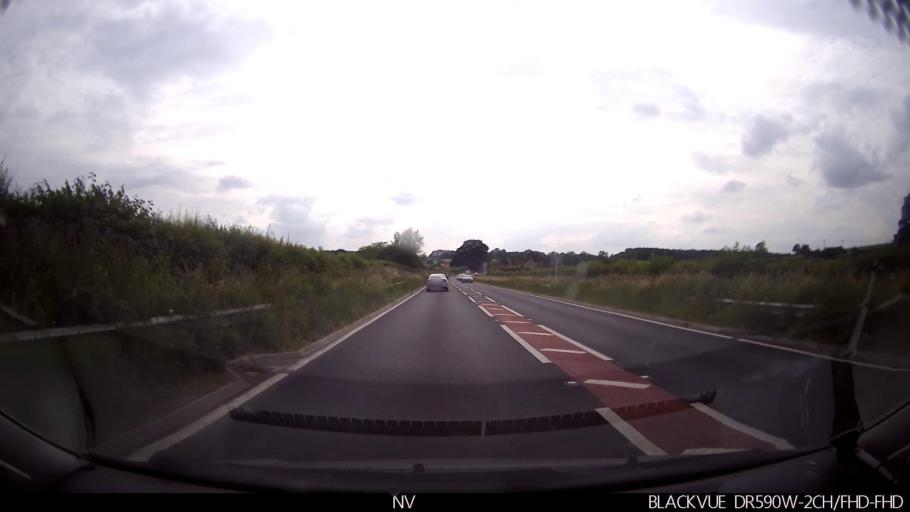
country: GB
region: England
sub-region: North Yorkshire
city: Huttons Ambo
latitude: 54.1183
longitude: -0.8309
